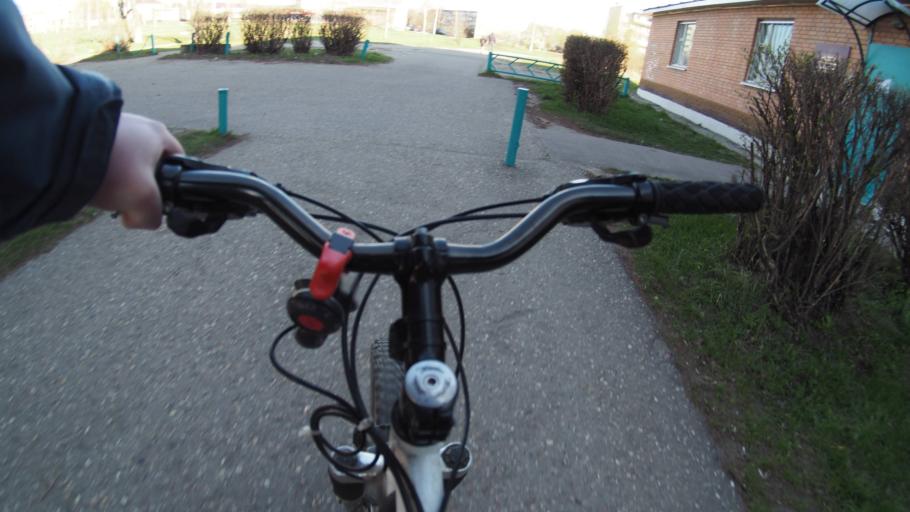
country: RU
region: Moskovskaya
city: Malyshevo
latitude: 55.5106
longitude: 38.3369
